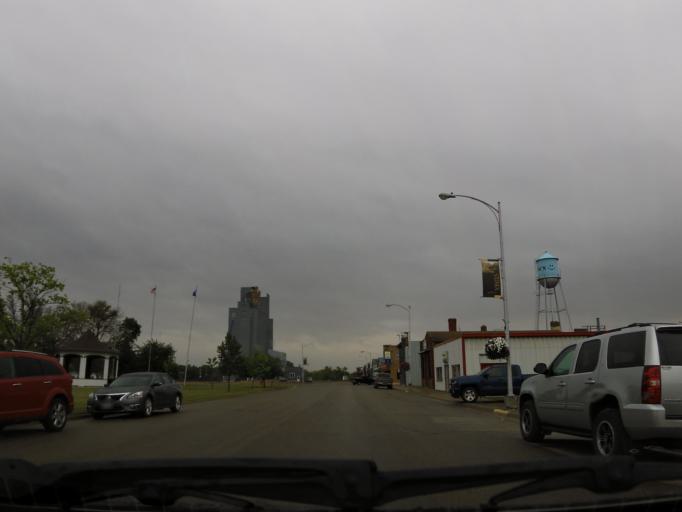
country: US
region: Minnesota
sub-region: Marshall County
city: Warren
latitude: 48.4511
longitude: -96.8746
